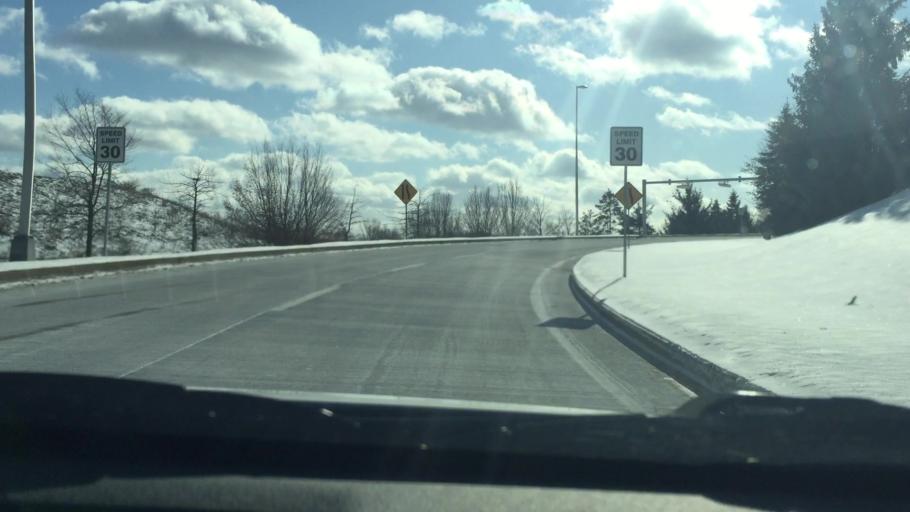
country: US
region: Pennsylvania
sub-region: Allegheny County
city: Carnot-Moon
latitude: 40.4941
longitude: -80.2555
